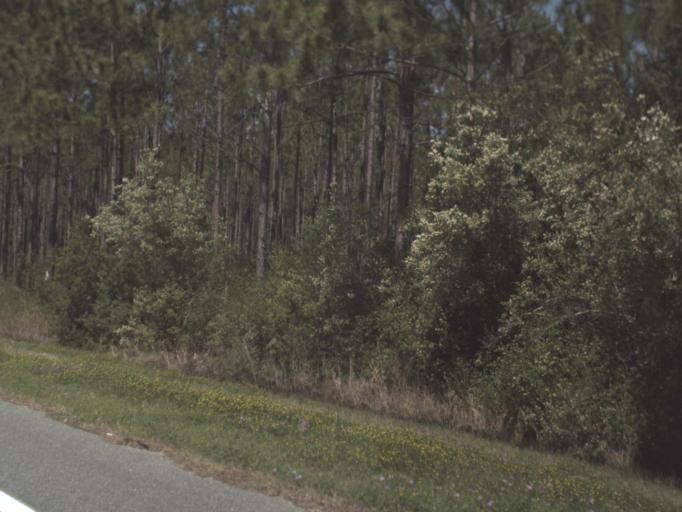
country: US
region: Florida
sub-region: Bay County
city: Lynn Haven
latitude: 30.3293
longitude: -85.7197
